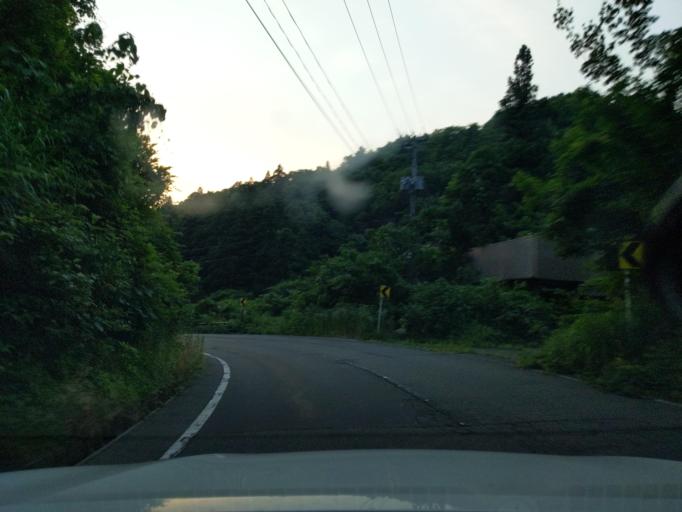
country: JP
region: Niigata
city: Kashiwazaki
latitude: 37.4532
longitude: 138.6327
